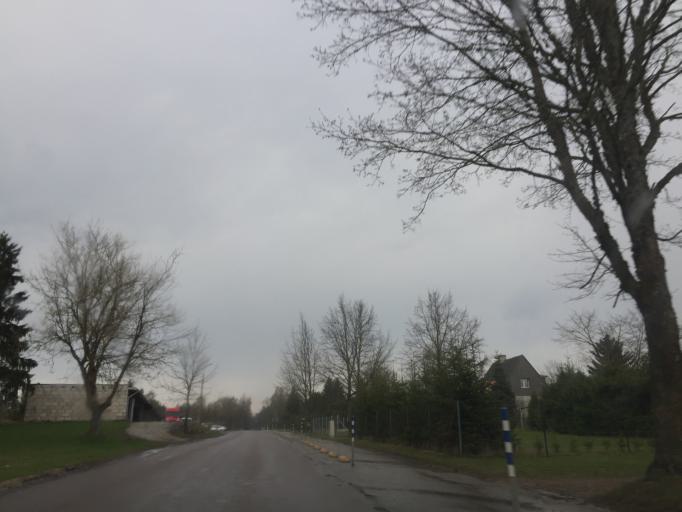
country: EE
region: Tartu
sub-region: UElenurme vald
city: Ulenurme
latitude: 58.3114
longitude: 26.7217
